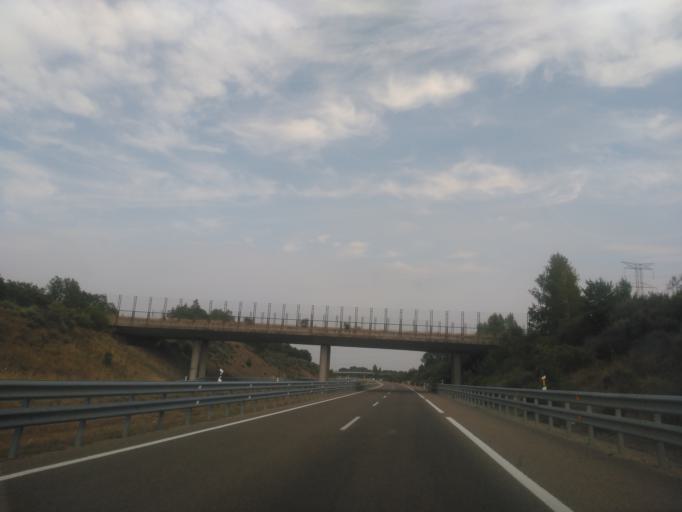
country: ES
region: Castille and Leon
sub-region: Provincia de Zamora
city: Cernadilla
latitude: 42.0321
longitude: -6.4260
